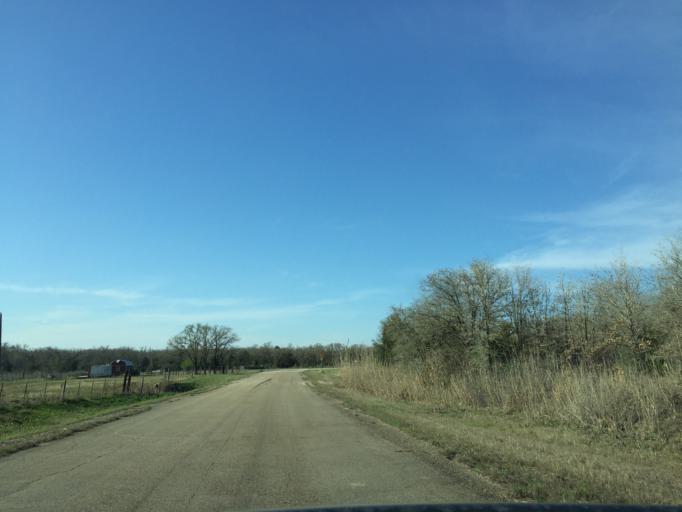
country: US
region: Texas
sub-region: Lee County
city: Lexington
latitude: 30.4655
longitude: -97.1477
